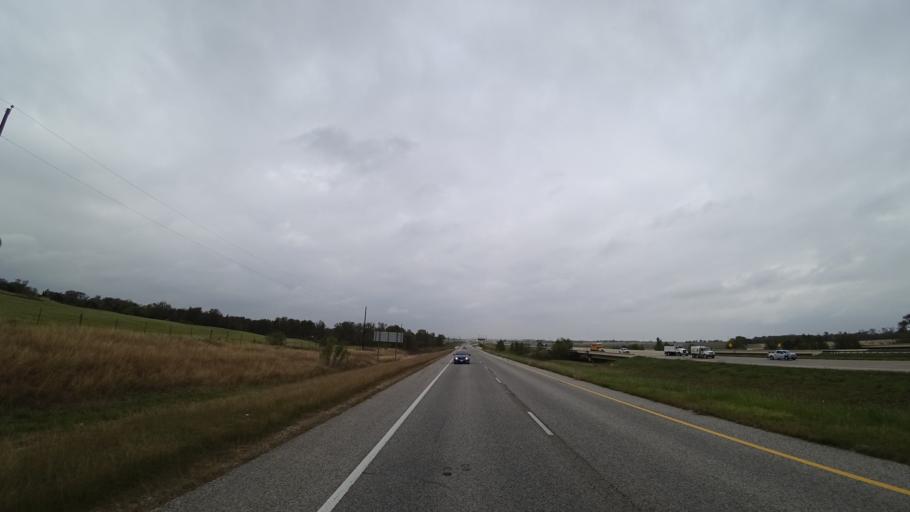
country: US
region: Texas
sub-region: Travis County
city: Pflugerville
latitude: 30.4280
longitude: -97.5900
